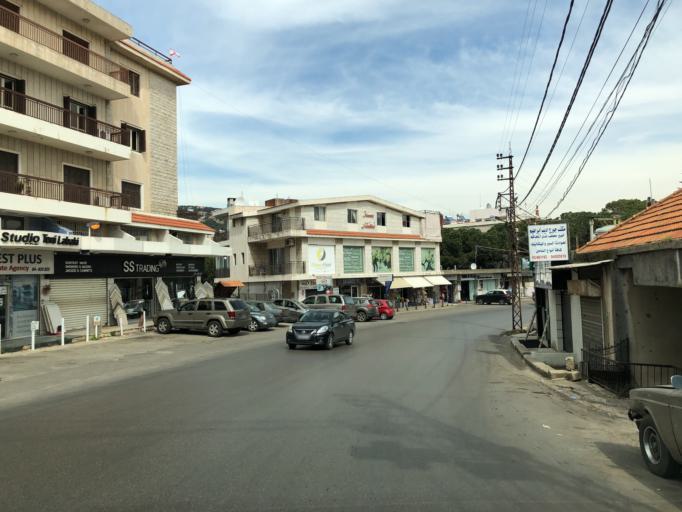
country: LB
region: Mont-Liban
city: Bhamdoun el Mhatta
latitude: 33.8891
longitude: 35.6576
